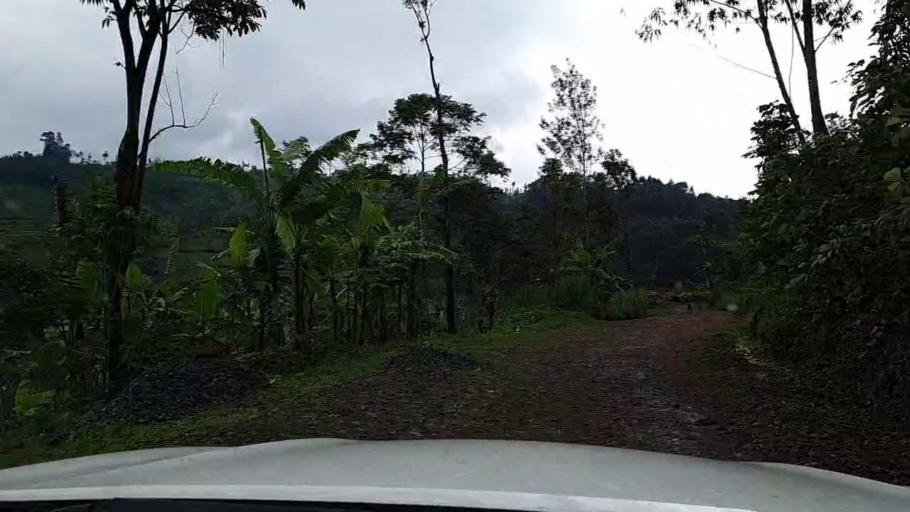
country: RW
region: Western Province
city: Cyangugu
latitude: -2.5400
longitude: 29.0393
